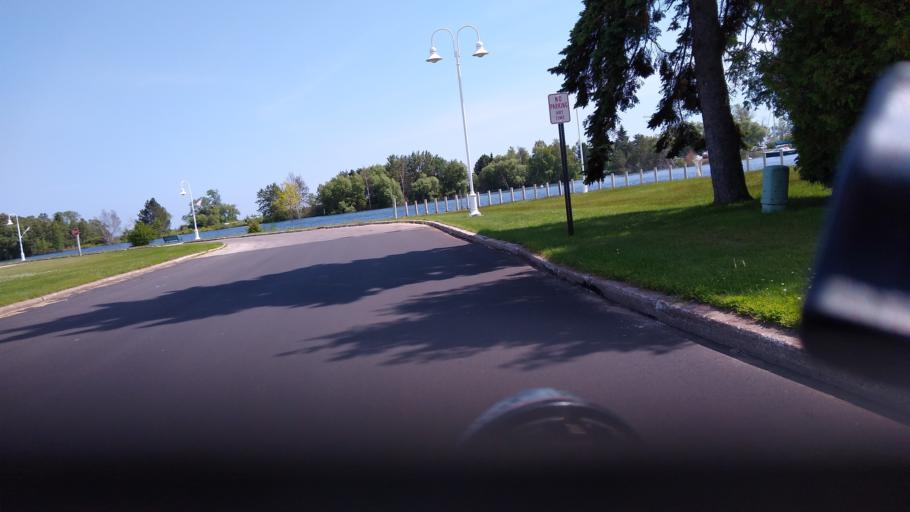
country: US
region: Michigan
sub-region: Delta County
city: Escanaba
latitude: 45.7439
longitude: -87.0423
